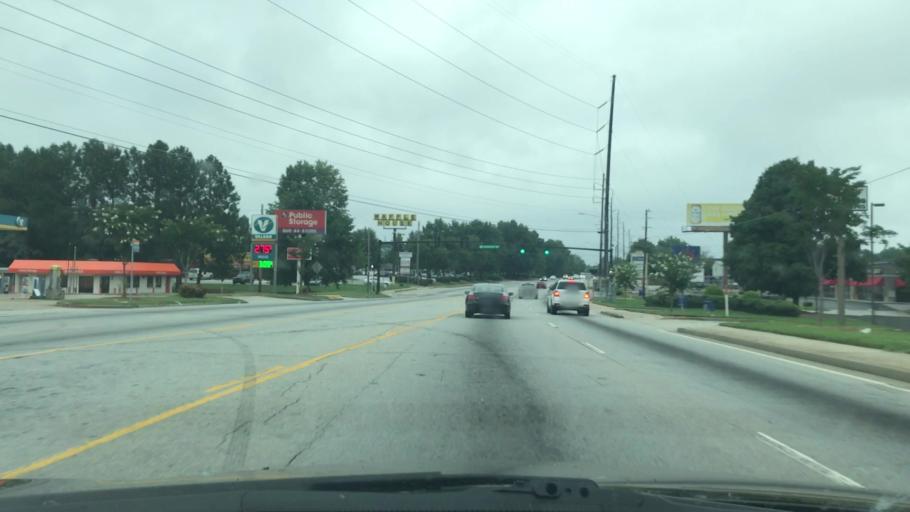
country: US
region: Georgia
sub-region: DeKalb County
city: Tucker
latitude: 33.8366
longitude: -84.2007
